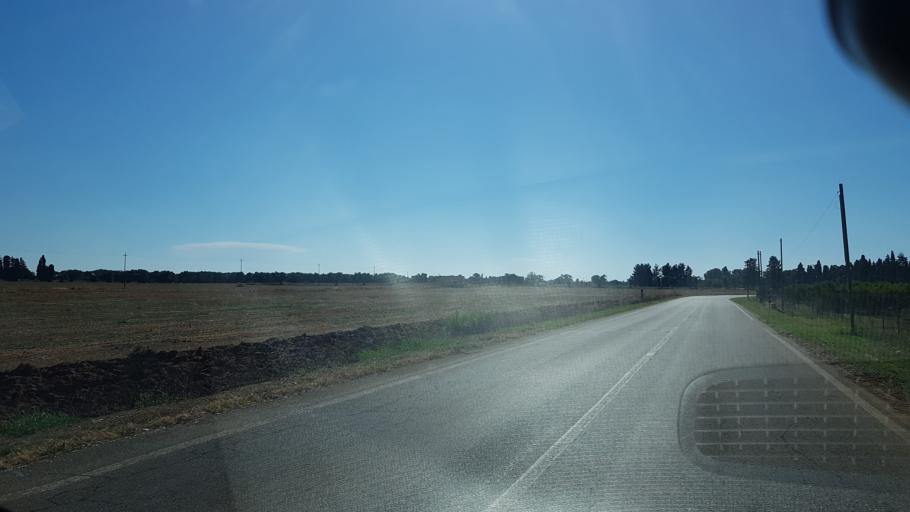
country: IT
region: Apulia
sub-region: Provincia di Brindisi
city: Mesagne
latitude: 40.5569
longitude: 17.8511
